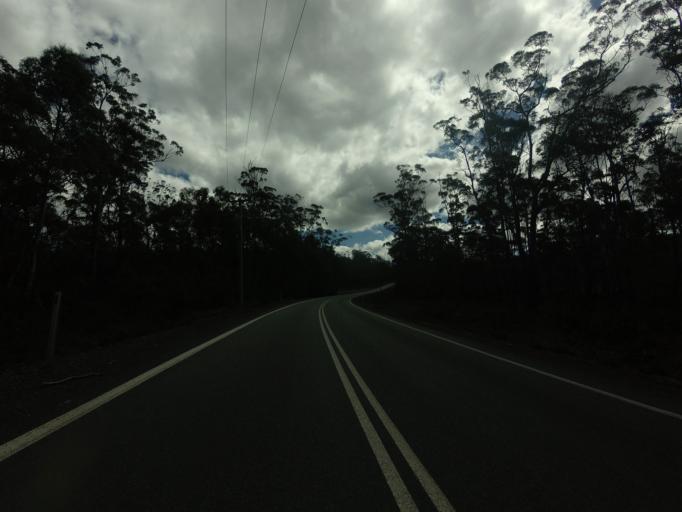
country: AU
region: Tasmania
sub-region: Northern Midlands
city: Evandale
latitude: -42.0252
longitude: 147.7667
